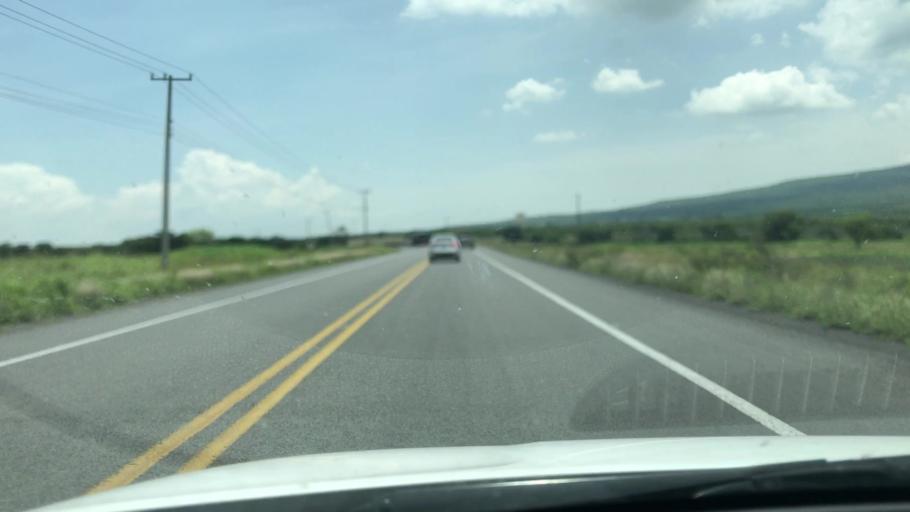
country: MX
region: Michoacan
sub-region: Yurecuaro
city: Yurecuaro
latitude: 20.3421
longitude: -102.1659
